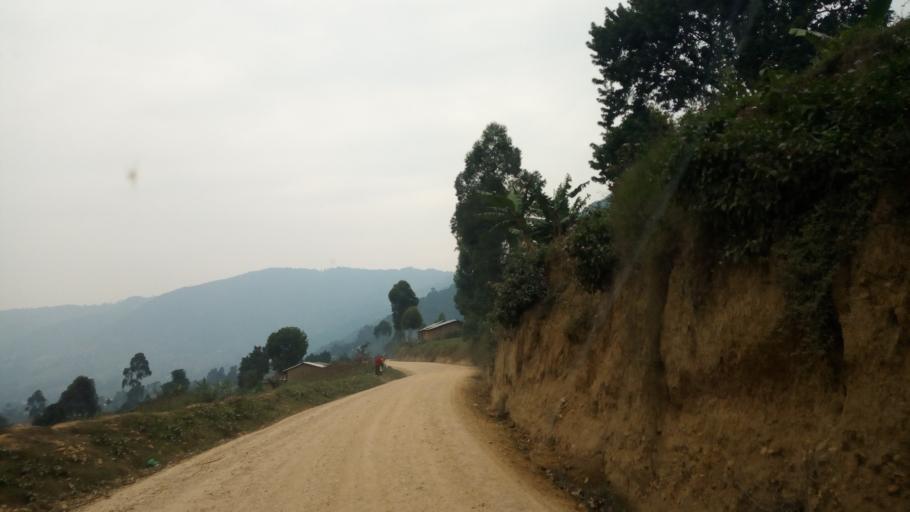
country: UG
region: Western Region
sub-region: Kanungu District
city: Kanungu
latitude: -1.1102
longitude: 29.8662
